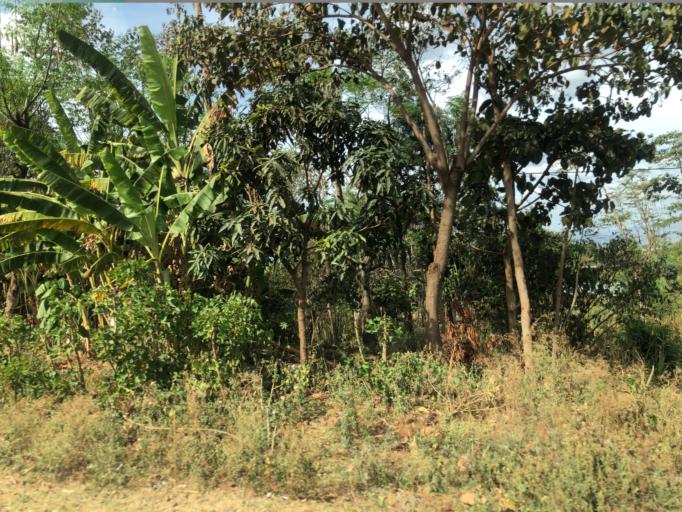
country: ET
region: Southern Nations, Nationalities, and People's Region
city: Konso
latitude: 5.3299
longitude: 37.4045
